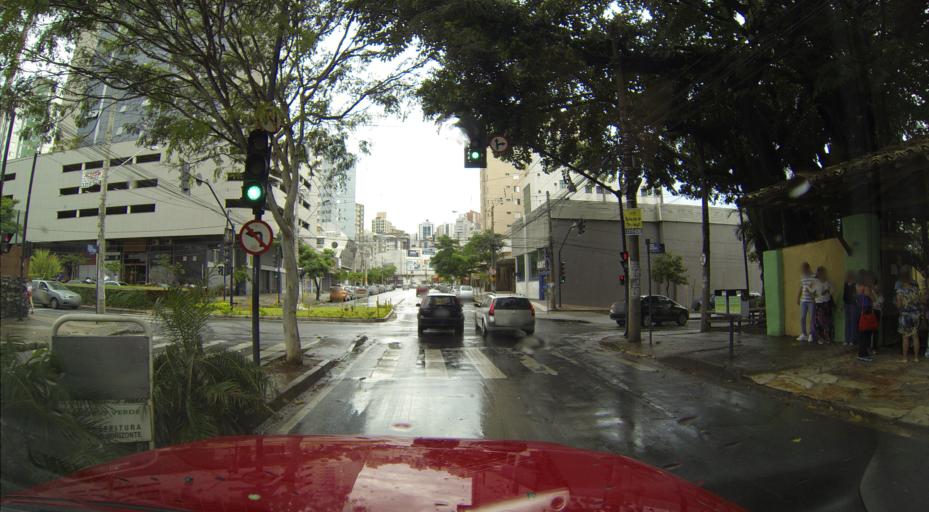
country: BR
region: Minas Gerais
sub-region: Belo Horizonte
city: Belo Horizonte
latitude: -19.9677
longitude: -43.9631
